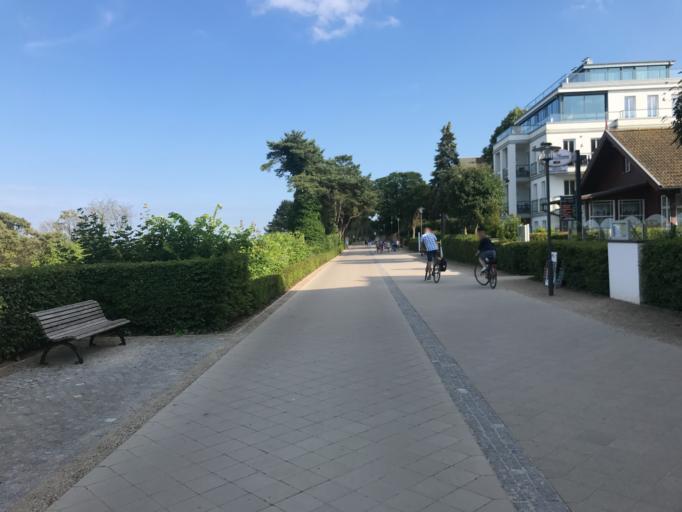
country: DE
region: Mecklenburg-Vorpommern
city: Seebad Bansin
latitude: 53.9704
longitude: 14.1481
